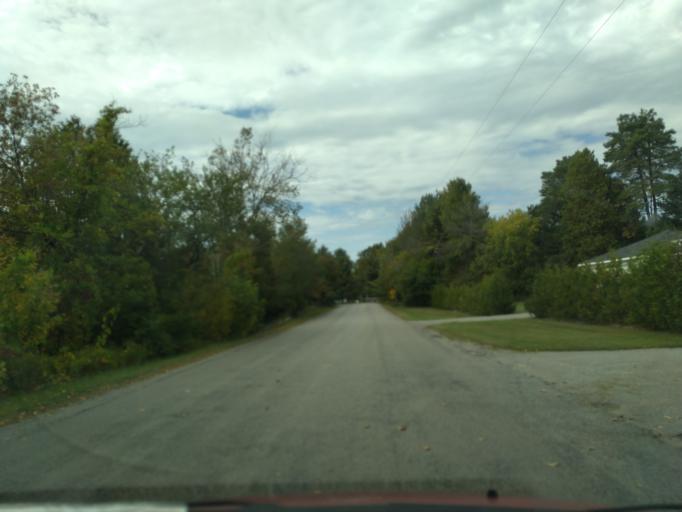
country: CA
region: Ontario
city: Keswick
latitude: 44.2633
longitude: -79.3577
